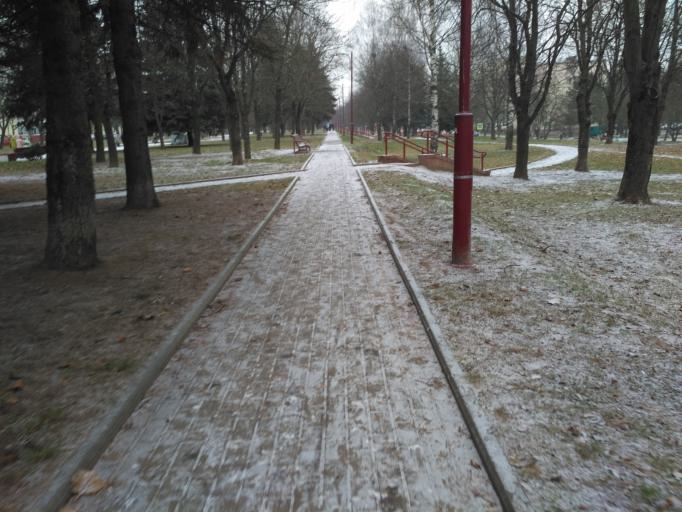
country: BY
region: Minsk
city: Novoye Medvezhino
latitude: 53.9109
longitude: 27.4881
